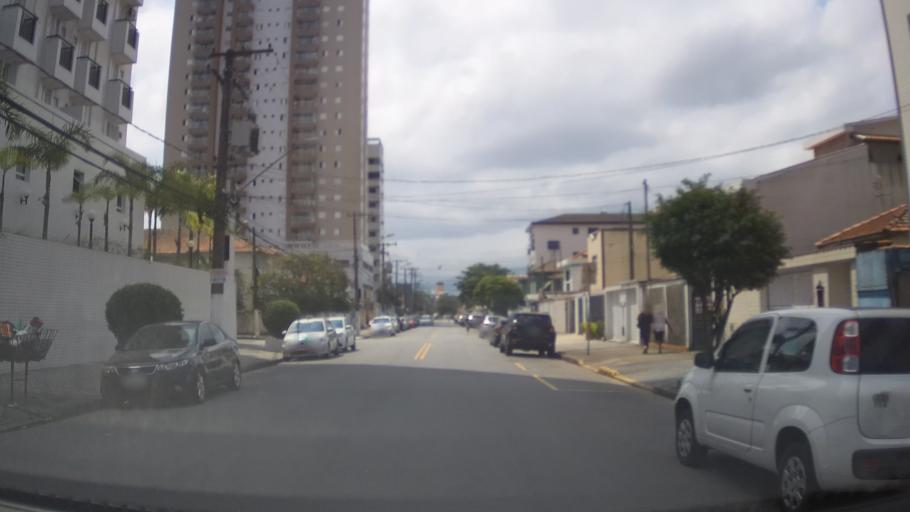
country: BR
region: Sao Paulo
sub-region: Santos
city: Santos
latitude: -23.9634
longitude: -46.3116
